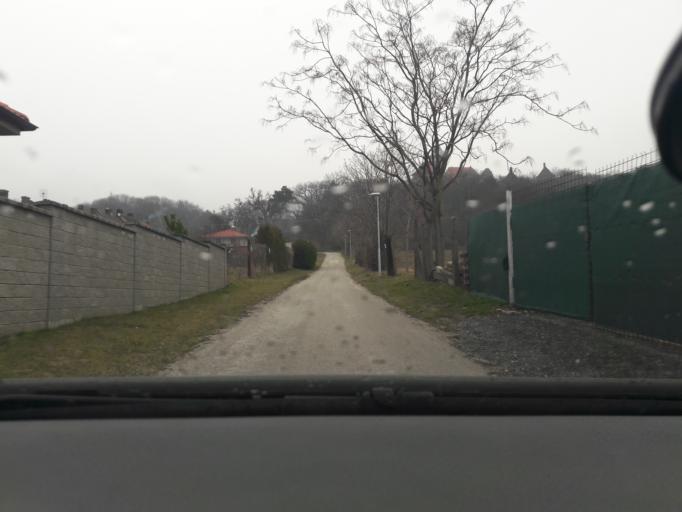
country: SK
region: Trnavsky
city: Smolenice
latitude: 48.5105
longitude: 17.4361
